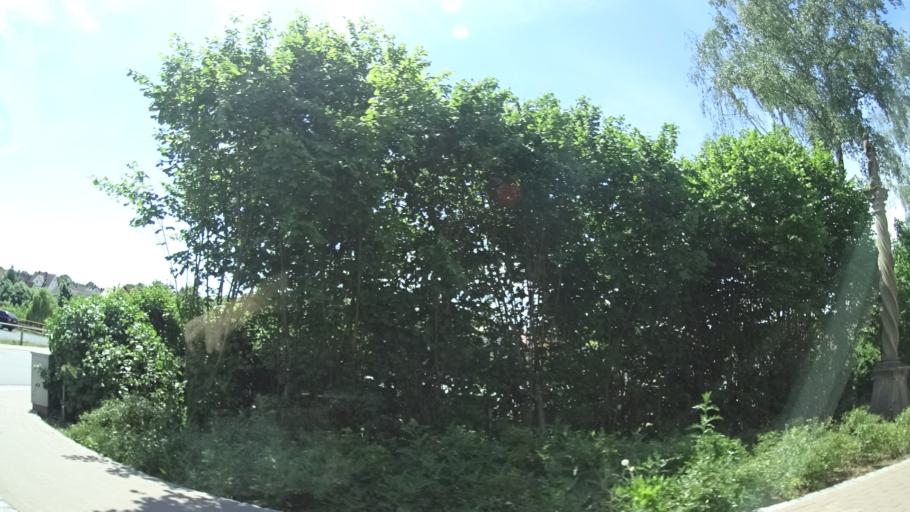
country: DE
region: Bavaria
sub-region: Regierungsbezirk Unterfranken
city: Poppenhausen
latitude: 50.1019
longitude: 10.1428
